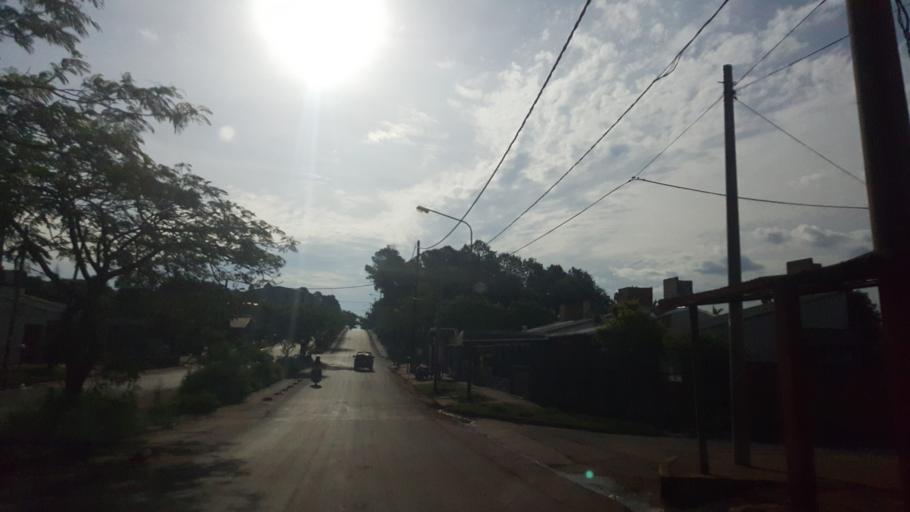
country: AR
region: Misiones
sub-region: Departamento de Capital
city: Posadas
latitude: -27.4266
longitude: -55.9239
